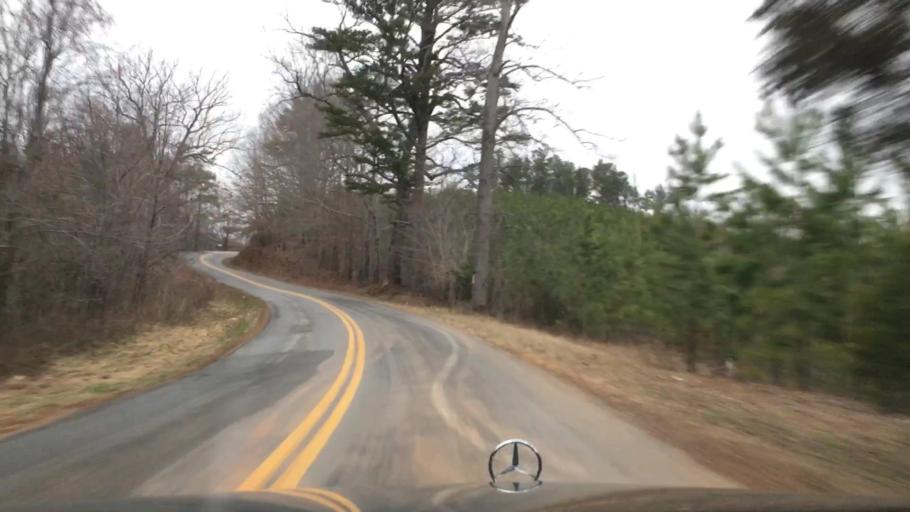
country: US
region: Virginia
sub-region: Pittsylvania County
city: Hurt
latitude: 37.1130
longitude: -79.3153
